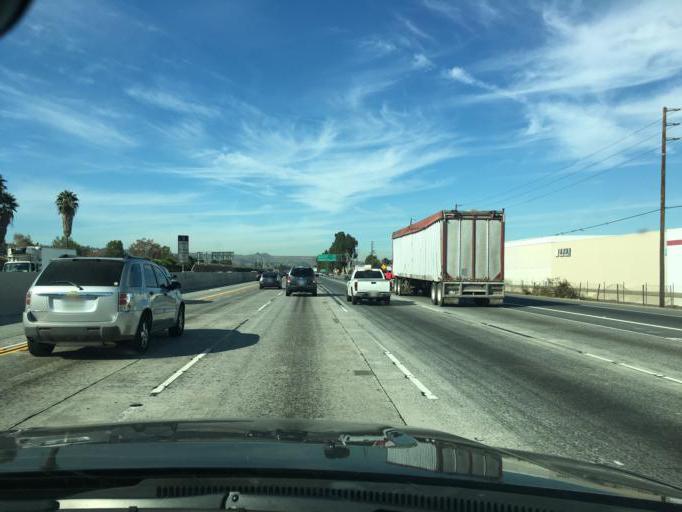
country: US
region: California
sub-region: Los Angeles County
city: La Puente
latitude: 33.9984
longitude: -117.9364
